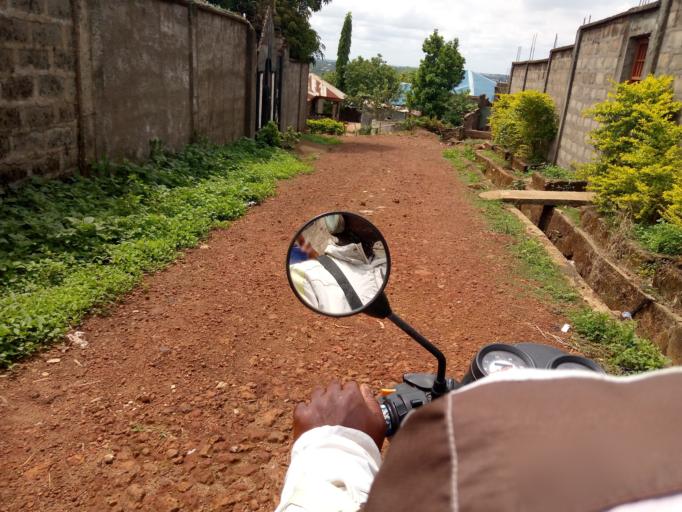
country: SL
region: Western Area
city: Waterloo
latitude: 8.3495
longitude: -13.0773
